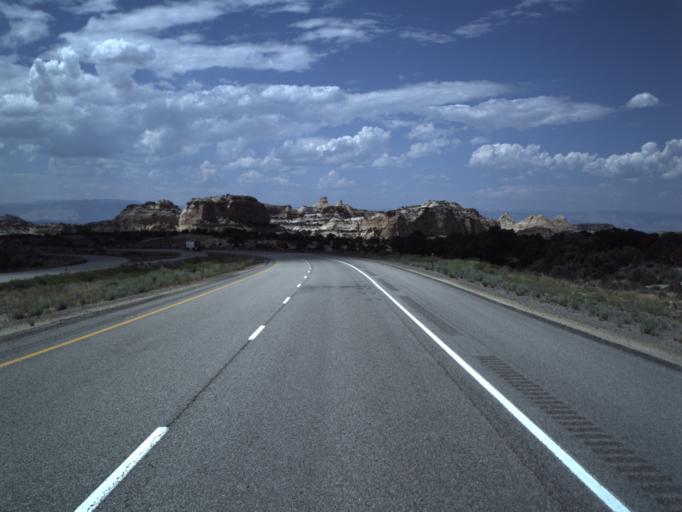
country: US
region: Utah
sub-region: Emery County
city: Ferron
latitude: 38.8622
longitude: -110.8425
